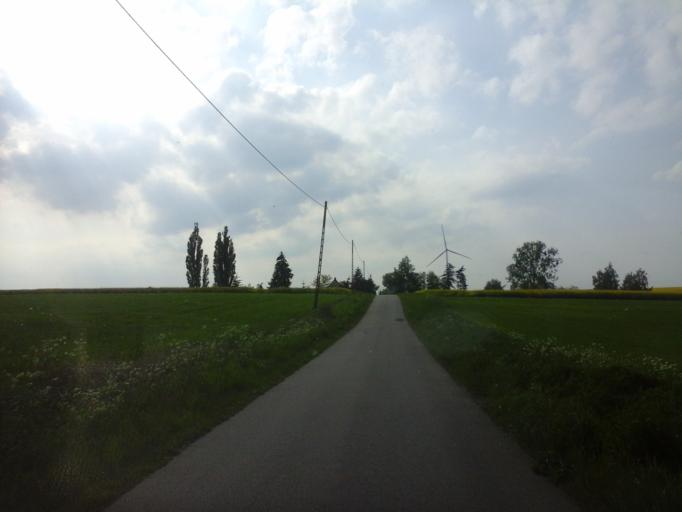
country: PL
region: West Pomeranian Voivodeship
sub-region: Powiat choszczenski
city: Pelczyce
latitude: 53.0301
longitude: 15.2758
